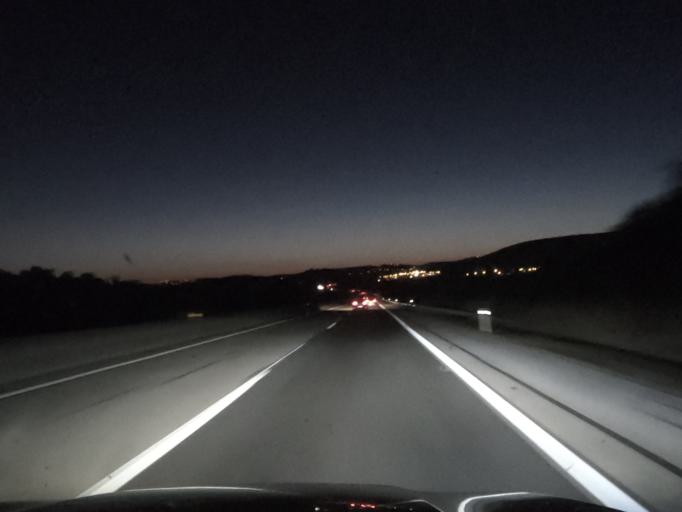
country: PT
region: Faro
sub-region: Loule
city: Vilamoura
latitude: 37.1259
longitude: -8.0883
